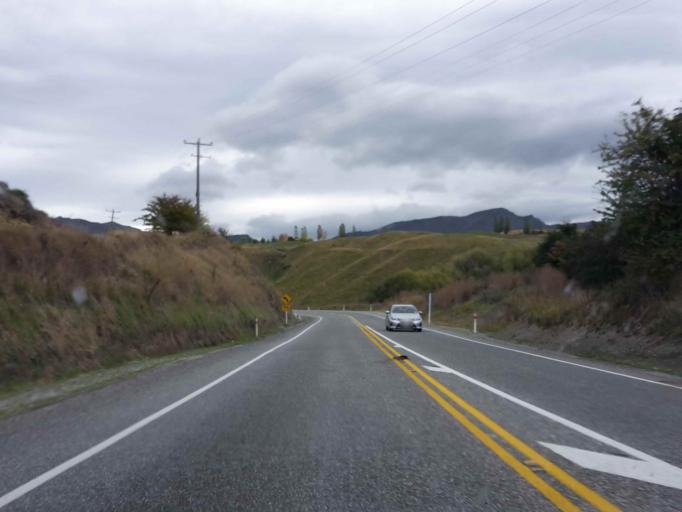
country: NZ
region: Otago
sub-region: Queenstown-Lakes District
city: Arrowtown
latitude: -44.9810
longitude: 168.8352
